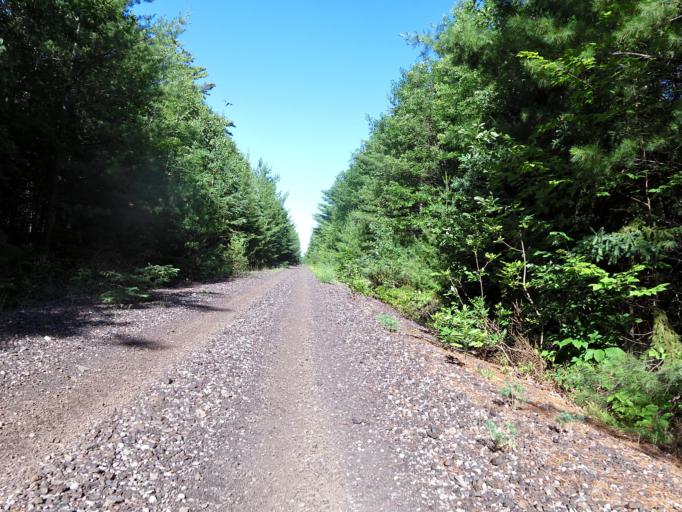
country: CA
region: Ontario
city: Arnprior
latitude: 45.4588
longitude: -76.2482
